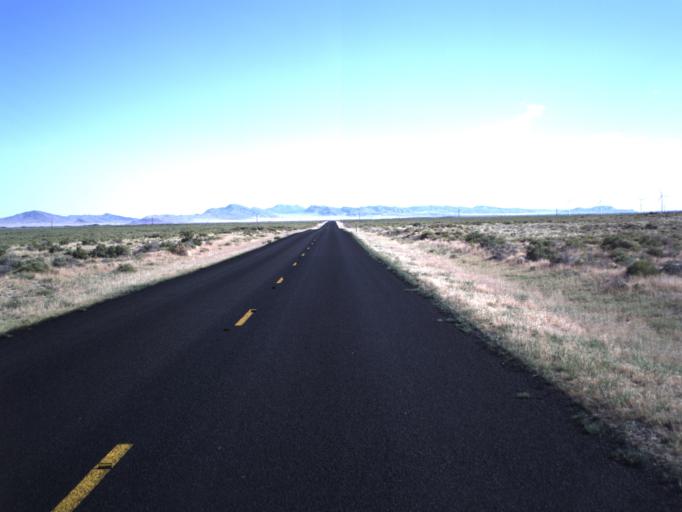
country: US
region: Utah
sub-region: Beaver County
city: Milford
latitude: 38.5446
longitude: -112.9912
